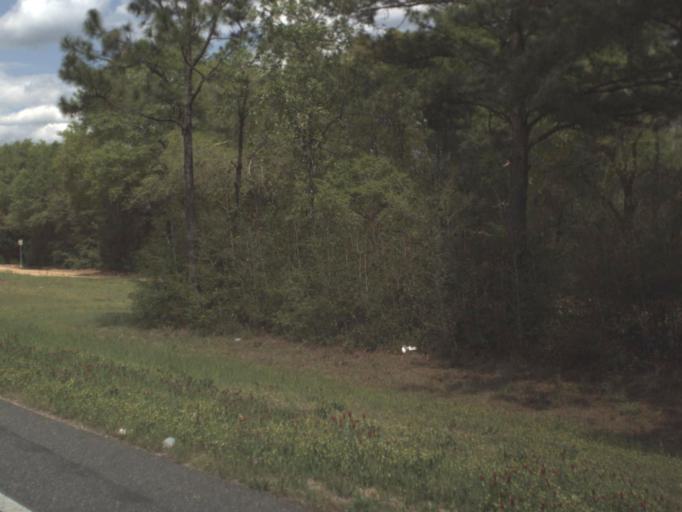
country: US
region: Florida
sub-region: Okaloosa County
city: Crestview
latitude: 30.8306
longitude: -86.5338
